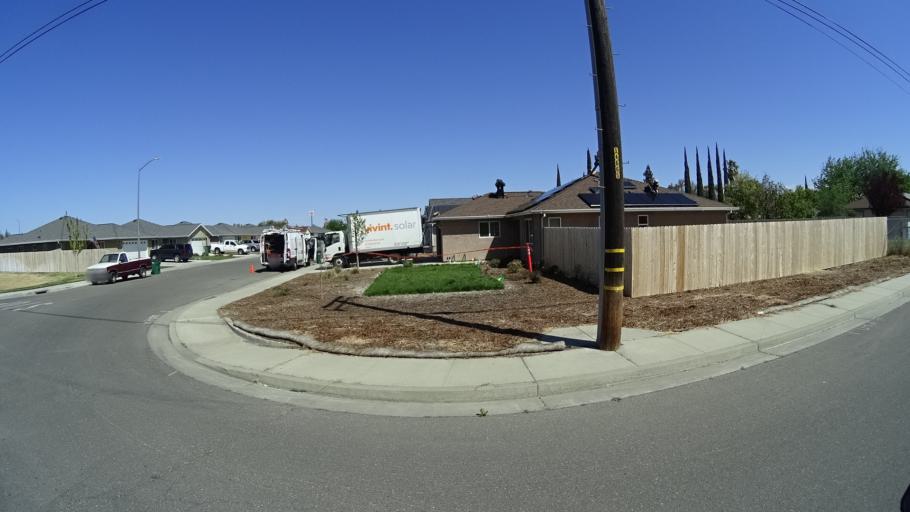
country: US
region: California
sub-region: Glenn County
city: Orland
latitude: 39.7439
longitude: -122.2038
